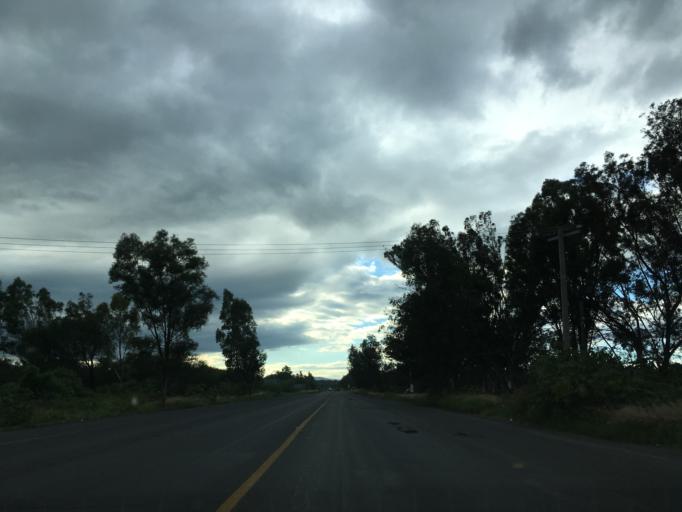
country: MX
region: Michoacan
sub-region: Cuitzeo
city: Cuamio
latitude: 20.0794
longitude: -101.1395
